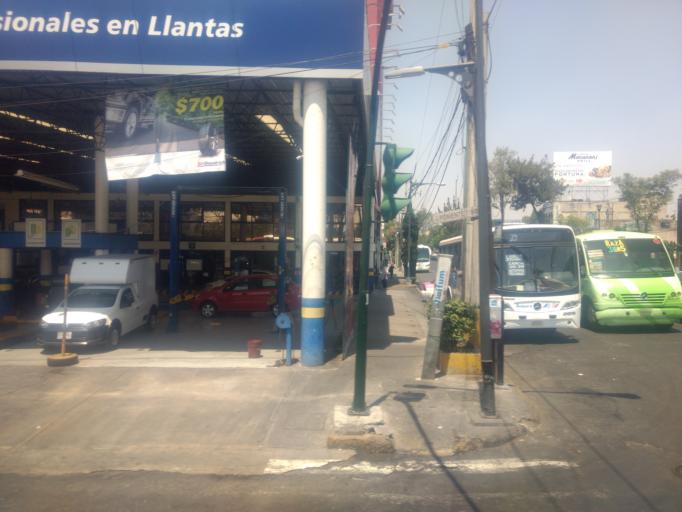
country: MX
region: Mexico
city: Colonia Lindavista
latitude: 19.4794
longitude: -99.1361
